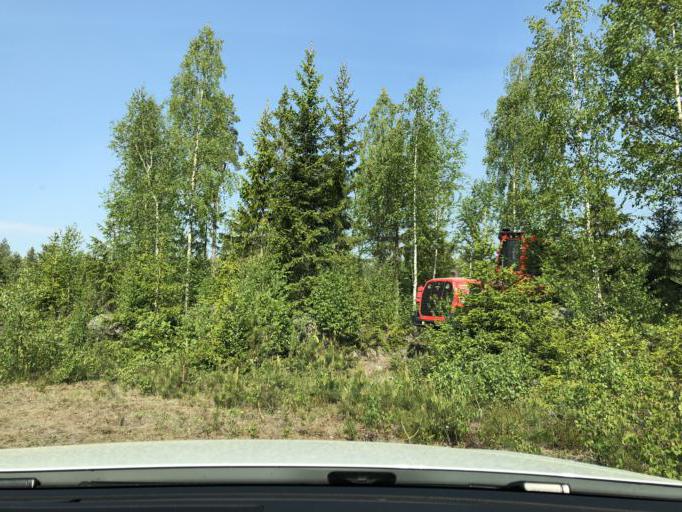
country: SE
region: Dalarna
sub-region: Avesta Kommun
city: Horndal
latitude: 60.2246
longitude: 16.5127
